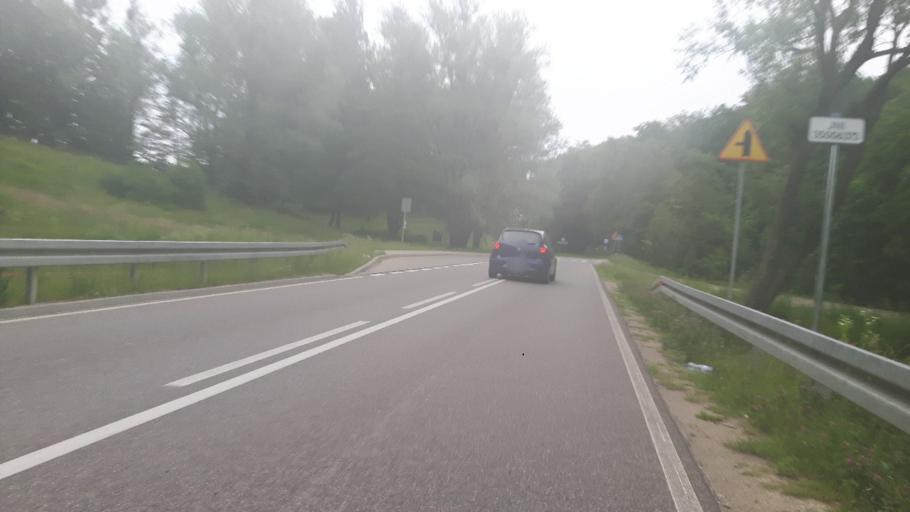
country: PL
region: Pomeranian Voivodeship
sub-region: Powiat nowodworski
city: Krynica Morska
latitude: 54.2686
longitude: 19.4194
